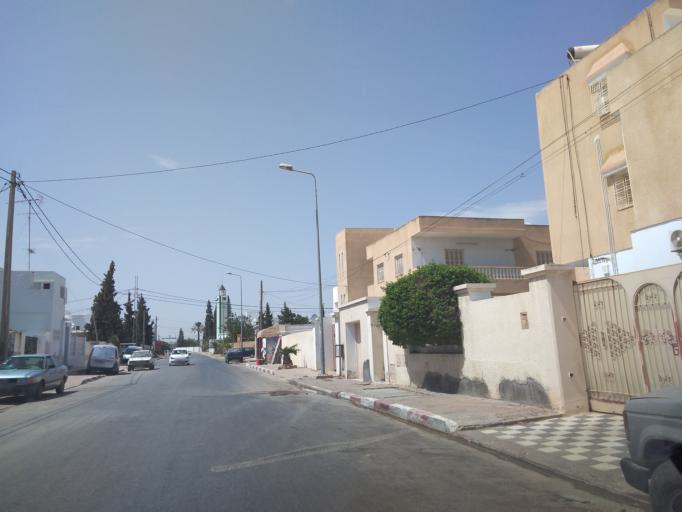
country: TN
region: Safaqis
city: Sfax
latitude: 34.7609
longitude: 10.7491
